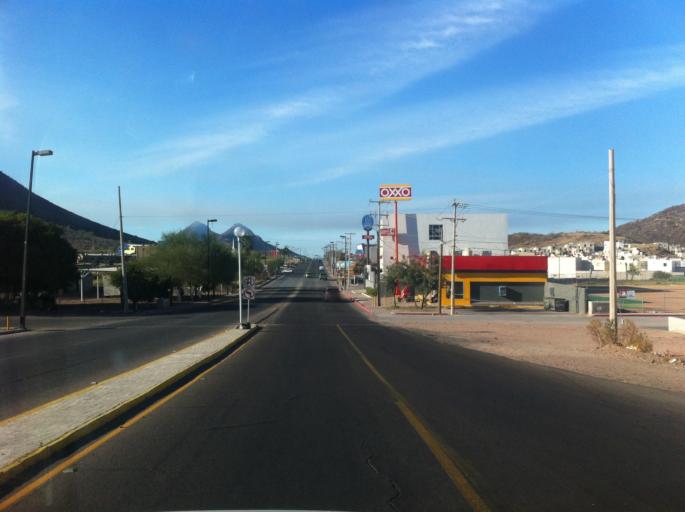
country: MX
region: Sonora
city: Heroica Guaymas
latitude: 27.9298
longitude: -110.9265
